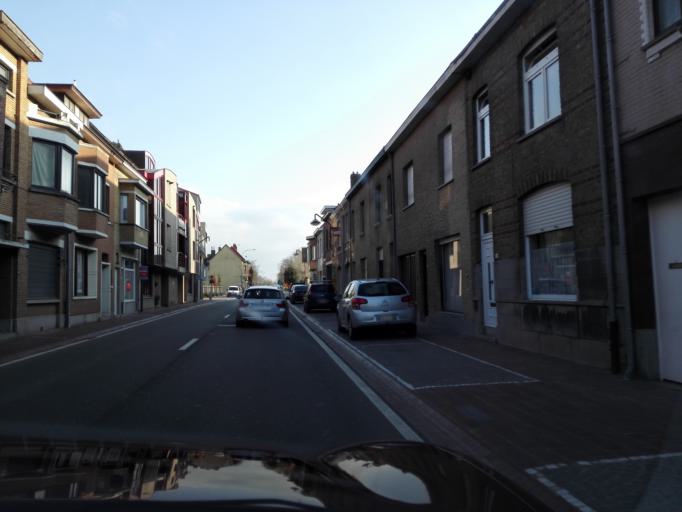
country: BE
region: Flanders
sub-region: Provincie West-Vlaanderen
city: De Panne
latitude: 51.0765
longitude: 2.6032
